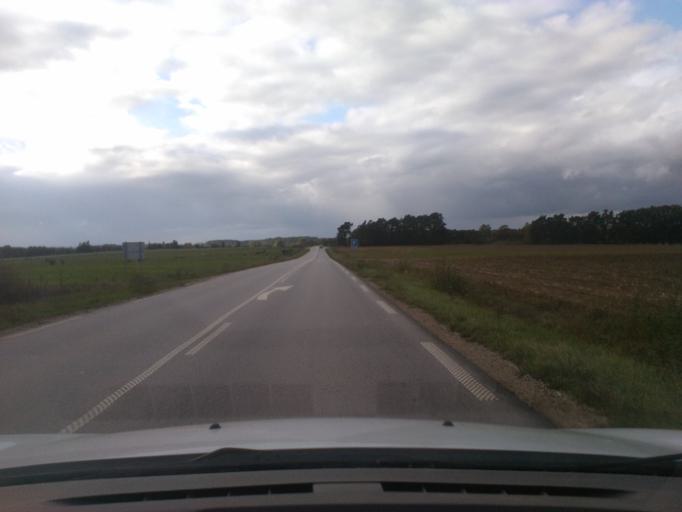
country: FR
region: Lorraine
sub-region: Departement des Vosges
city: Aydoilles
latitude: 48.2432
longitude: 6.6416
